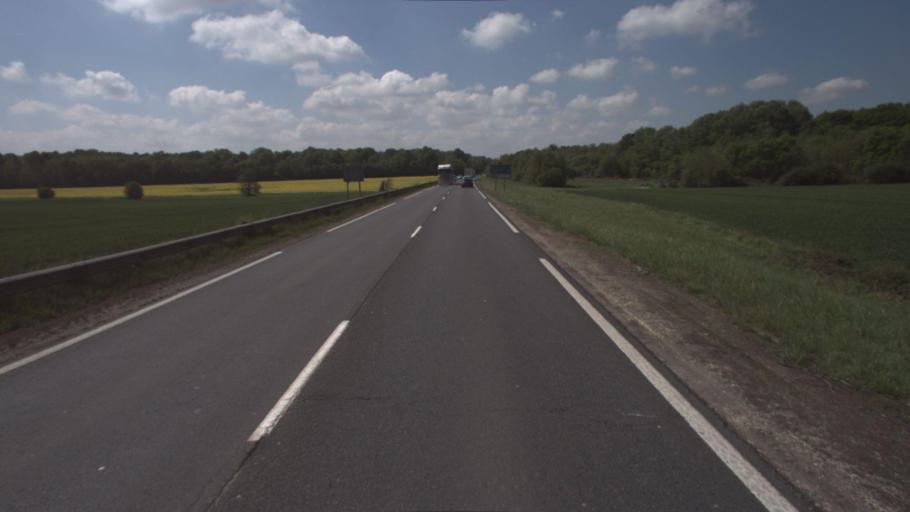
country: FR
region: Ile-de-France
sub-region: Departement de Seine-et-Marne
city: Fontenay-Tresigny
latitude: 48.7131
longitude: 2.8429
